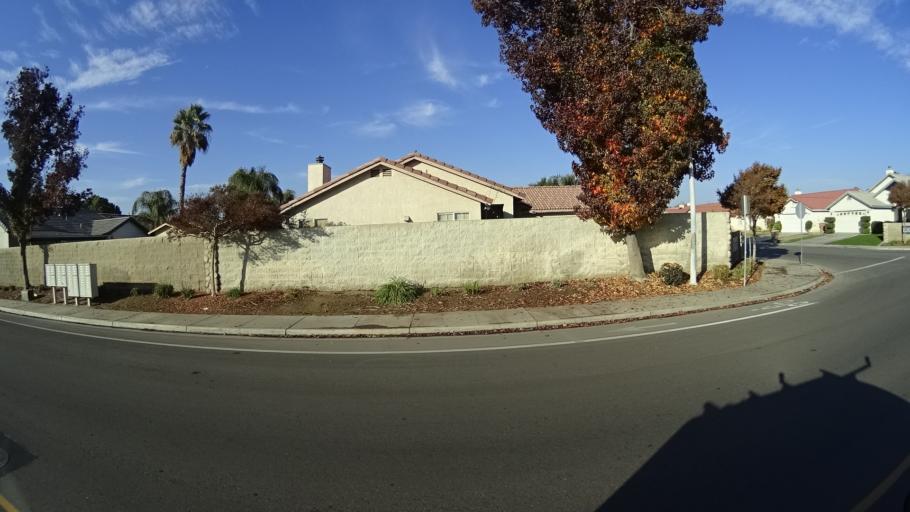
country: US
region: California
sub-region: Kern County
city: Greenfield
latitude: 35.2788
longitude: -119.0477
